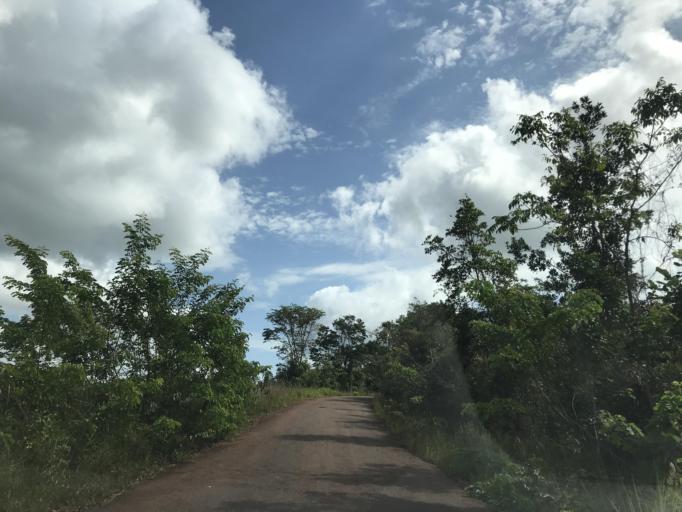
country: BR
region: Bahia
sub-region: Entre Rios
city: Entre Rios
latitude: -12.1721
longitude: -38.1118
